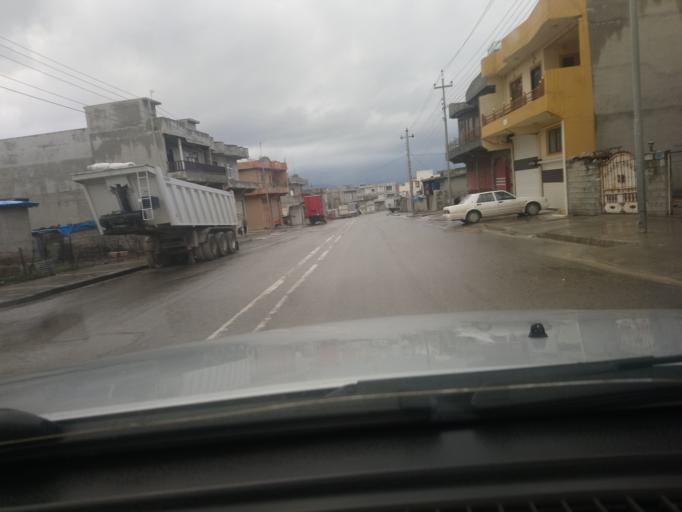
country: IQ
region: As Sulaymaniyah
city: Qeladize
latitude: 36.1784
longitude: 45.1432
